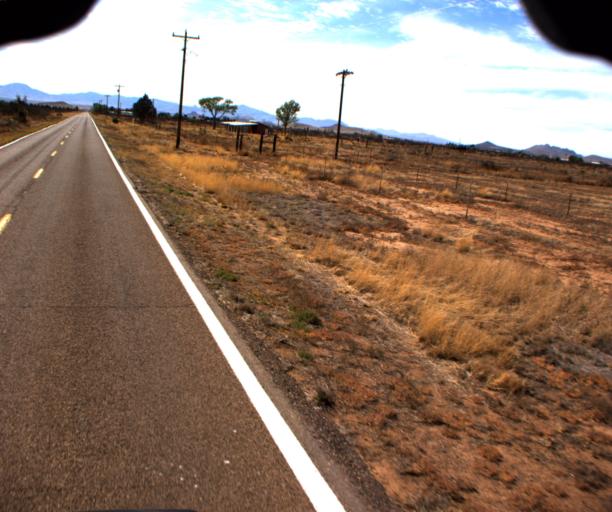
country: US
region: Arizona
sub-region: Cochise County
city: Willcox
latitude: 31.8762
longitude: -109.6247
